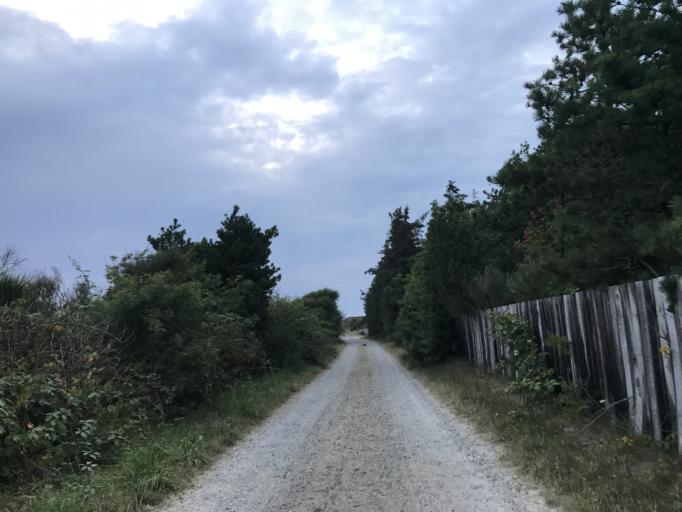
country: DK
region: South Denmark
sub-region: Faaborg-Midtfyn Kommune
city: Faaborg
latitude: 54.9355
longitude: 10.2440
